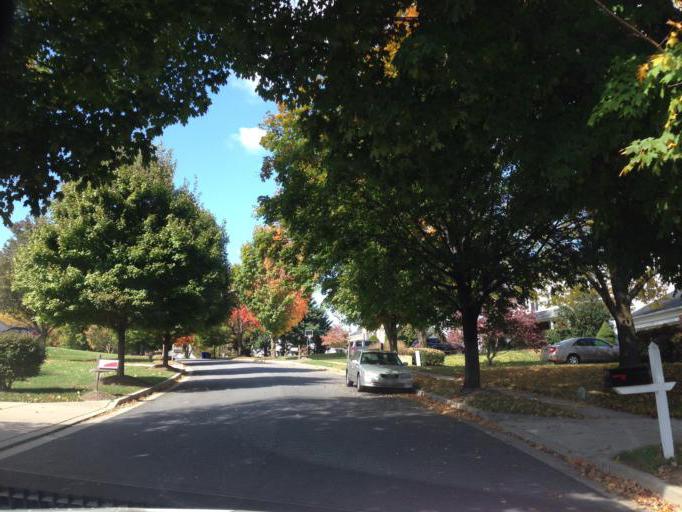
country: US
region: Maryland
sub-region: Howard County
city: Fulton
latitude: 39.1392
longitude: -76.8981
